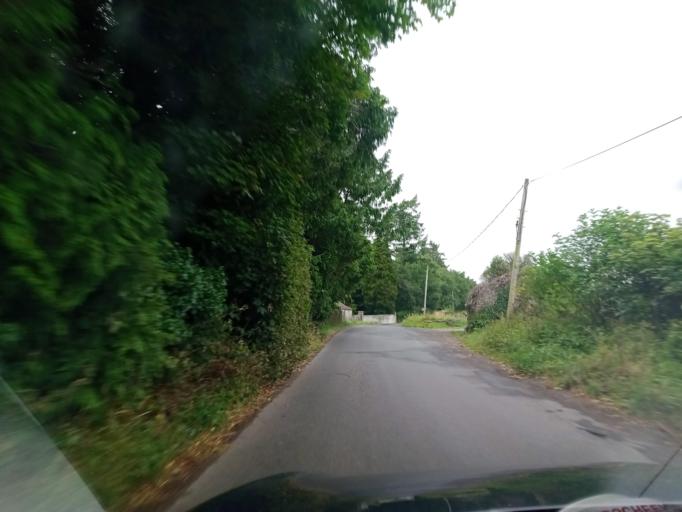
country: IE
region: Leinster
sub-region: Laois
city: Abbeyleix
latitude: 52.9264
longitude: -7.2814
